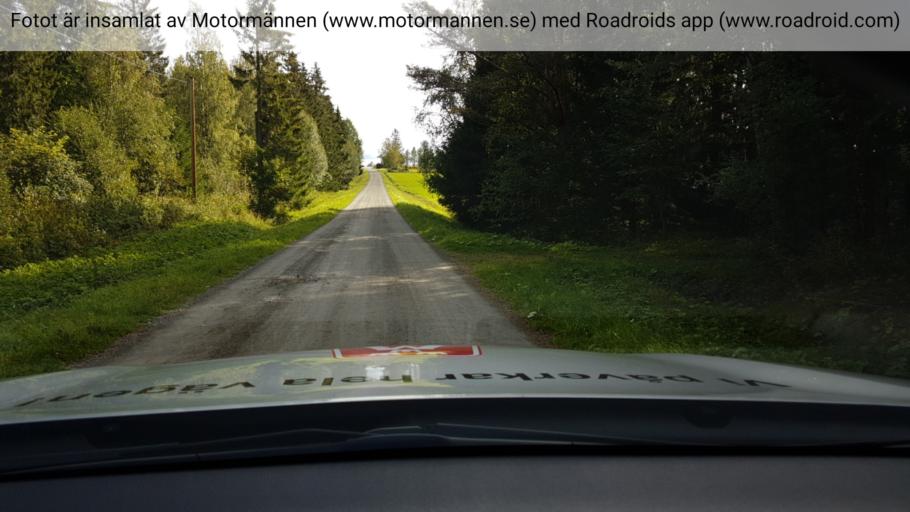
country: SE
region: Jaemtland
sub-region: Bergs Kommun
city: Hoverberg
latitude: 62.9363
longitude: 14.4150
